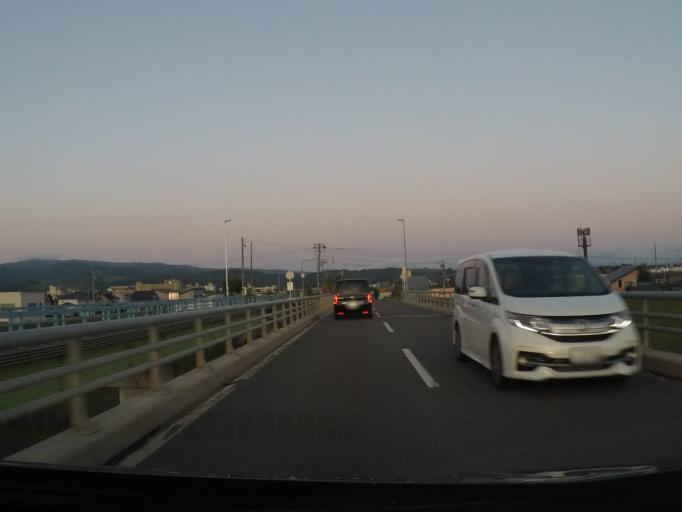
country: JP
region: Hokkaido
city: Nayoro
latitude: 44.3464
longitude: 142.4420
